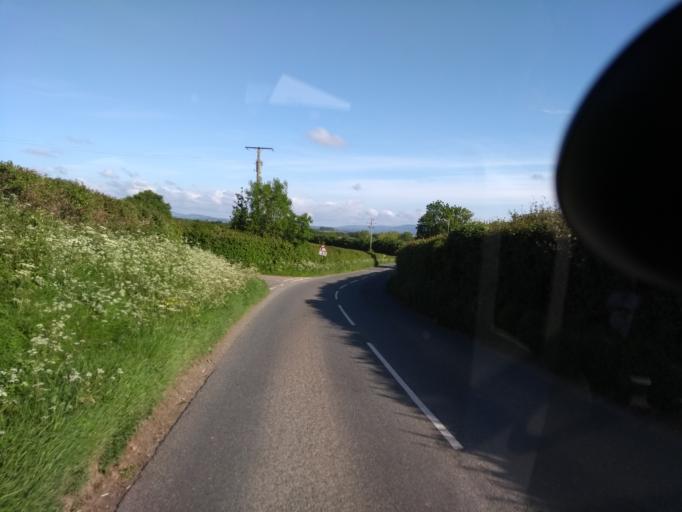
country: GB
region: England
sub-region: Somerset
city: Taunton
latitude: 50.9741
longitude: -3.1262
